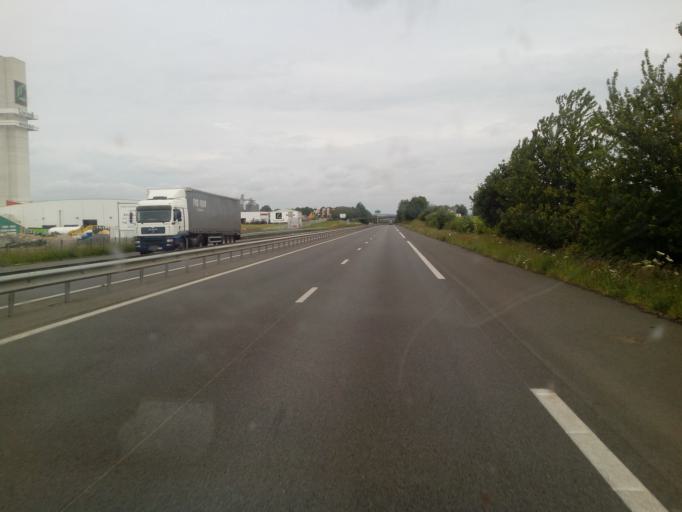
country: FR
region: Brittany
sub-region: Departement des Cotes-d'Armor
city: Broons
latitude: 48.3143
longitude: -2.2434
